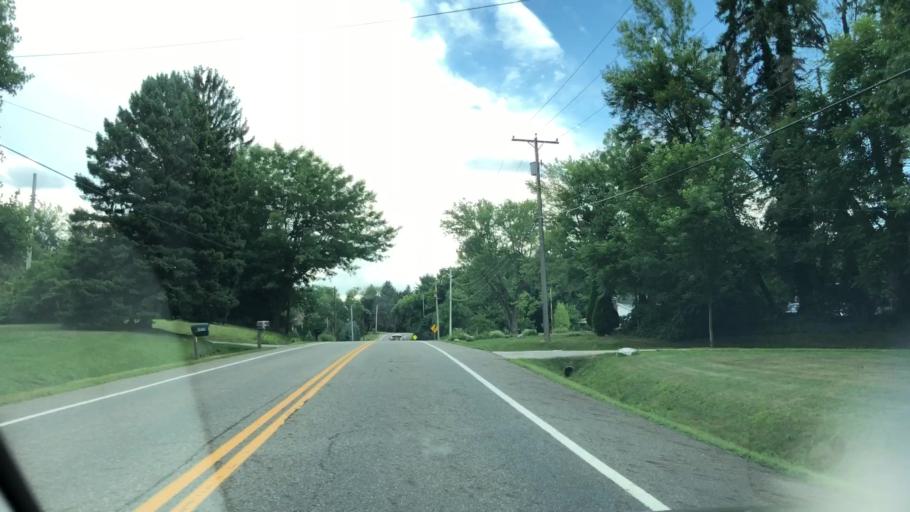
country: US
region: Ohio
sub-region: Summit County
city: Portage Lakes
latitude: 40.9924
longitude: -81.5517
